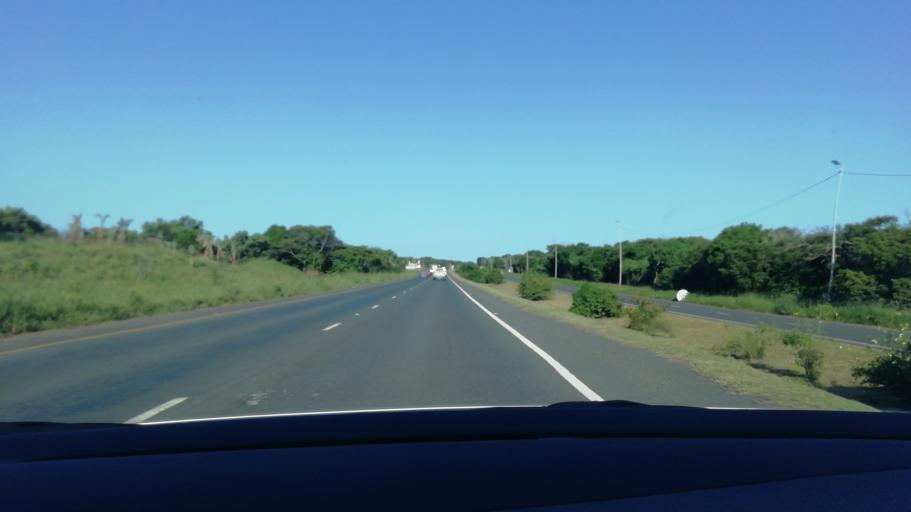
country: ZA
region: KwaZulu-Natal
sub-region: uThungulu District Municipality
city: Richards Bay
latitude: -28.7687
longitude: 32.0448
